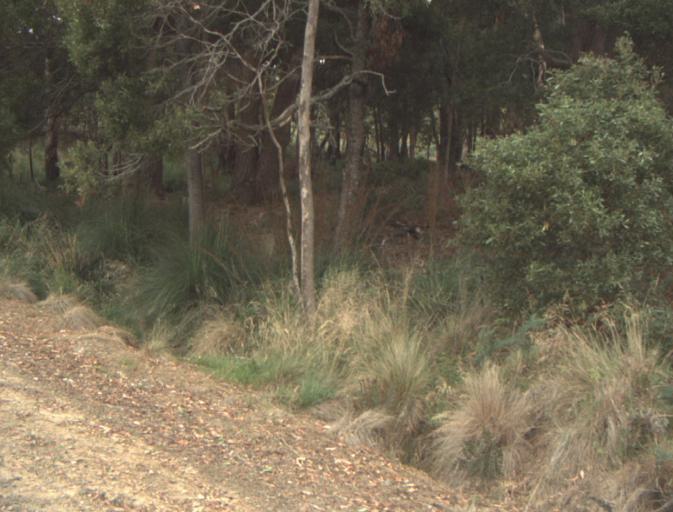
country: AU
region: Tasmania
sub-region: Northern Midlands
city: Evandale
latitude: -41.4576
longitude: 147.4642
